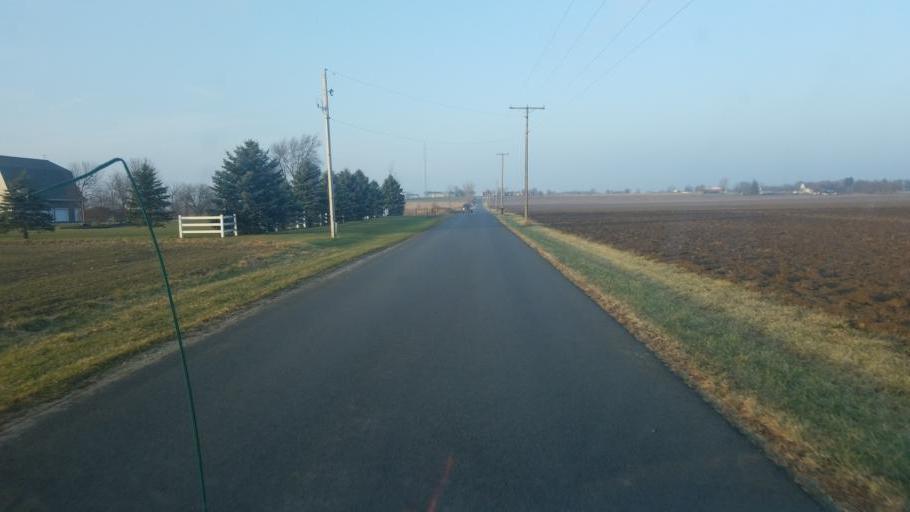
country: US
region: Ohio
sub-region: Wyandot County
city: Carey
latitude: 40.9546
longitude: -83.4292
